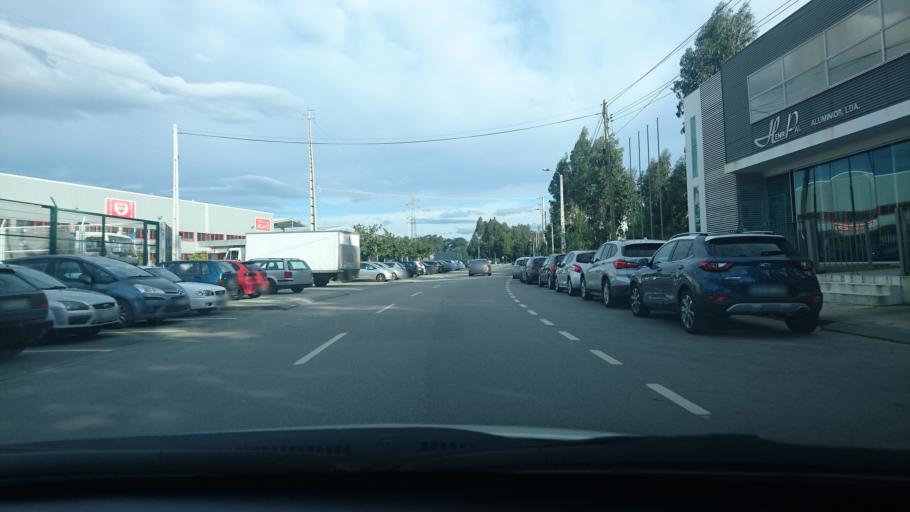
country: PT
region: Aveiro
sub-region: Ovar
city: Cortegaca
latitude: 40.9578
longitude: -8.6056
